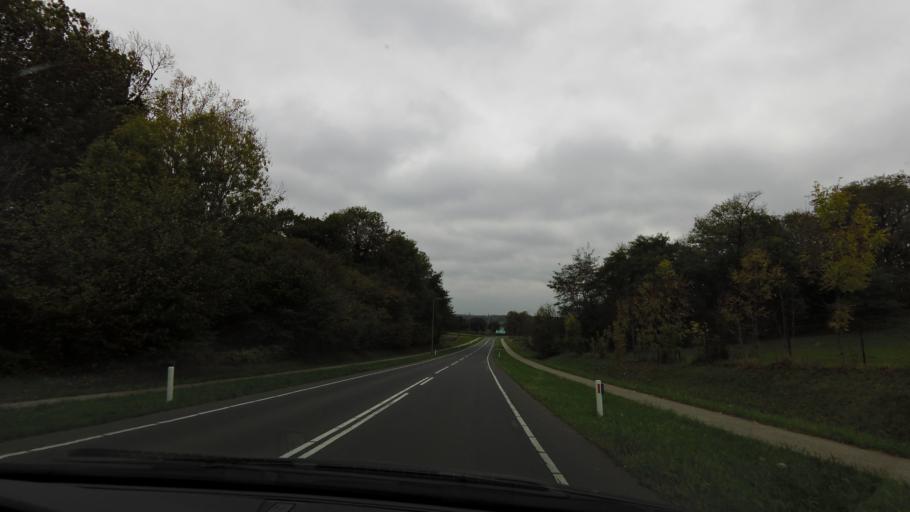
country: NL
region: Limburg
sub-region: Gemeente Schinnen
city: Puth
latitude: 50.9615
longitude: 5.8605
